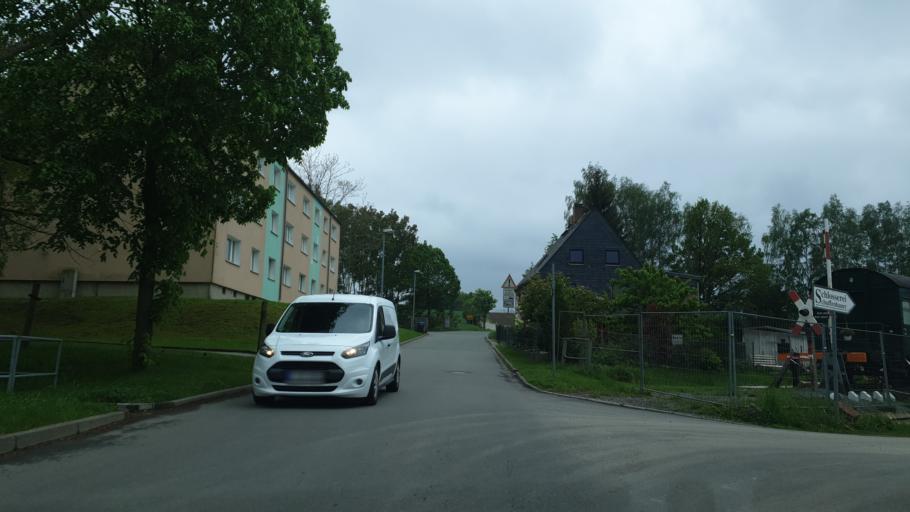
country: DE
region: Saxony
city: Hartmannsdorf
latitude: 50.8572
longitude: 12.8062
